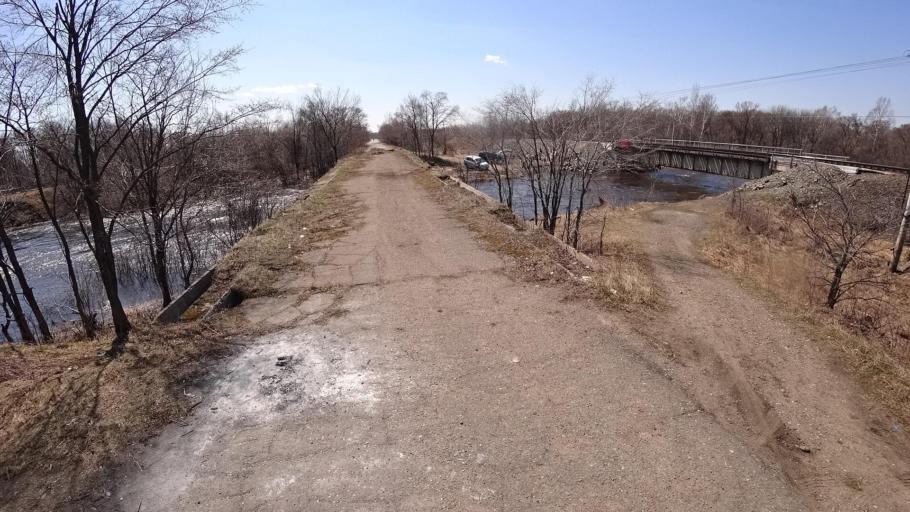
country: RU
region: Khabarovsk Krai
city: Khurba
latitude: 50.4004
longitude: 136.8651
